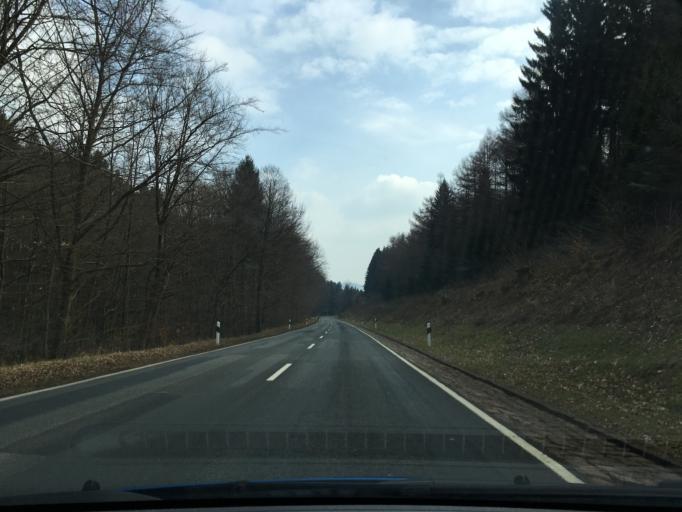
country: DE
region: Lower Saxony
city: Dassel
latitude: 51.7983
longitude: 9.6518
